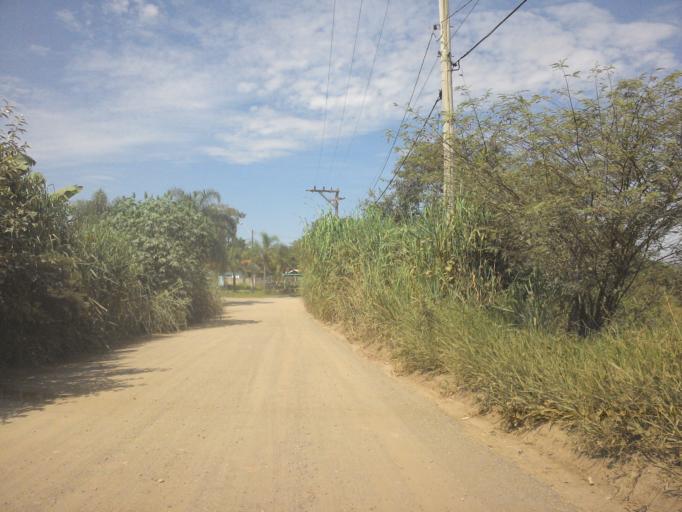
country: BR
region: Sao Paulo
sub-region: Valinhos
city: Valinhos
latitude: -22.9362
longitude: -46.9851
